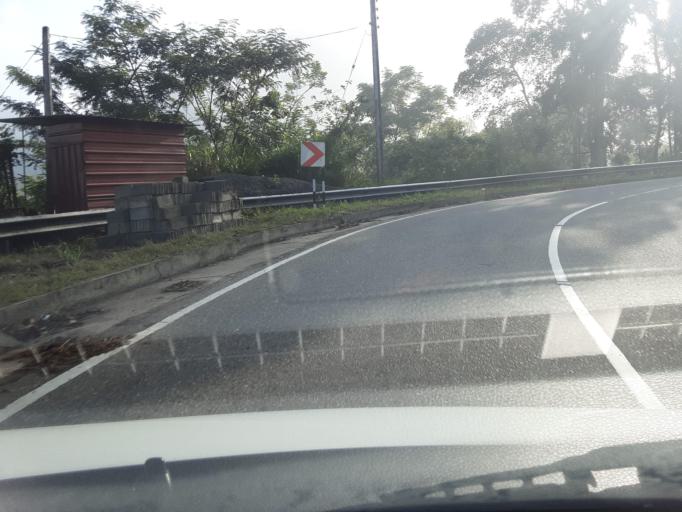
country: LK
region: Uva
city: Badulla
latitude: 6.9210
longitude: 80.9610
